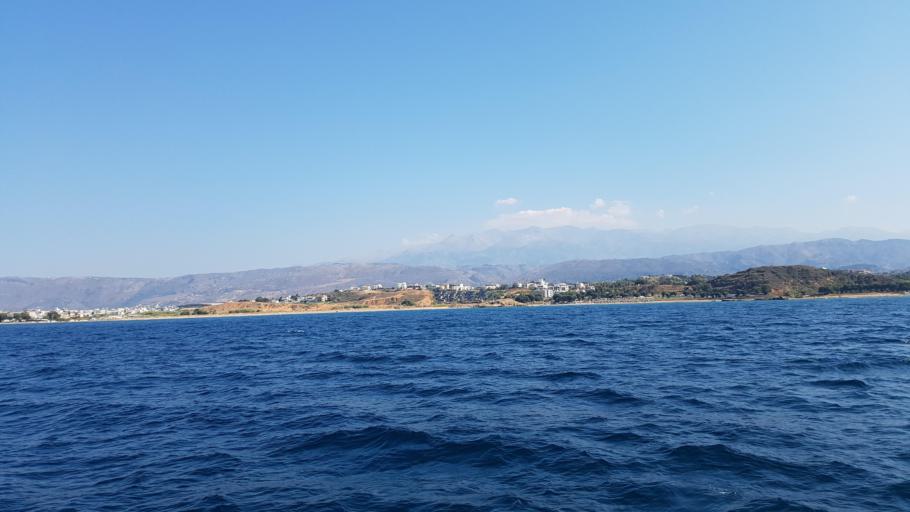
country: GR
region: Crete
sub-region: Nomos Chanias
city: Daratsos
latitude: 35.5185
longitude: 23.9933
